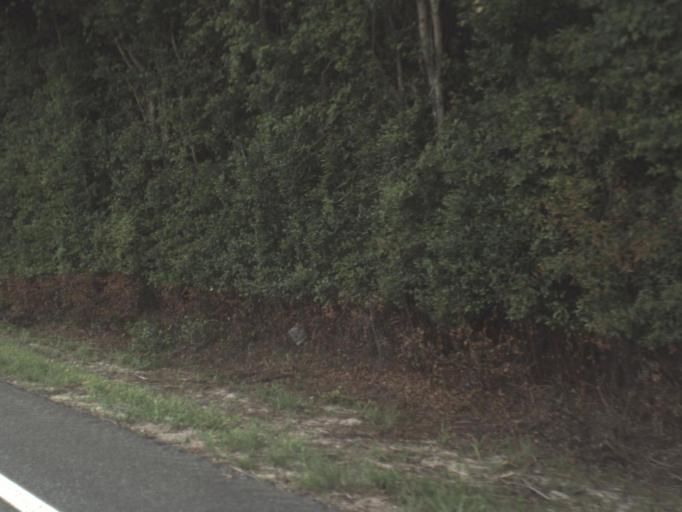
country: US
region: Florida
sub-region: Alachua County
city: Archer
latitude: 29.5798
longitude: -82.5509
